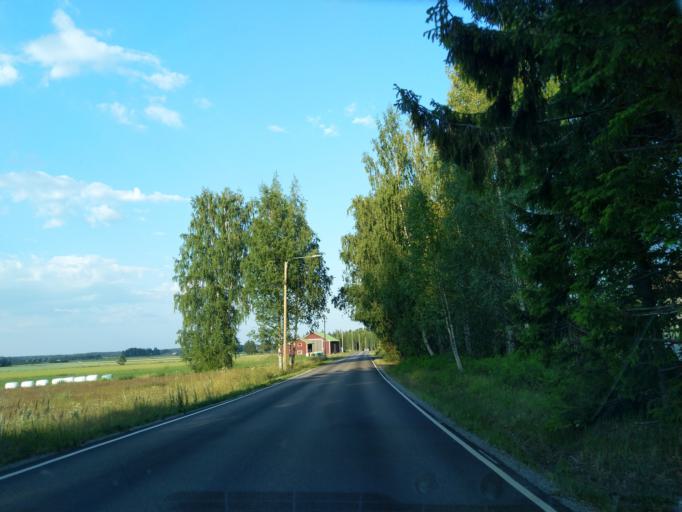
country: FI
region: Satakunta
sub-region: Pohjois-Satakunta
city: Kankaanpaeae
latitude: 61.8217
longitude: 22.2746
